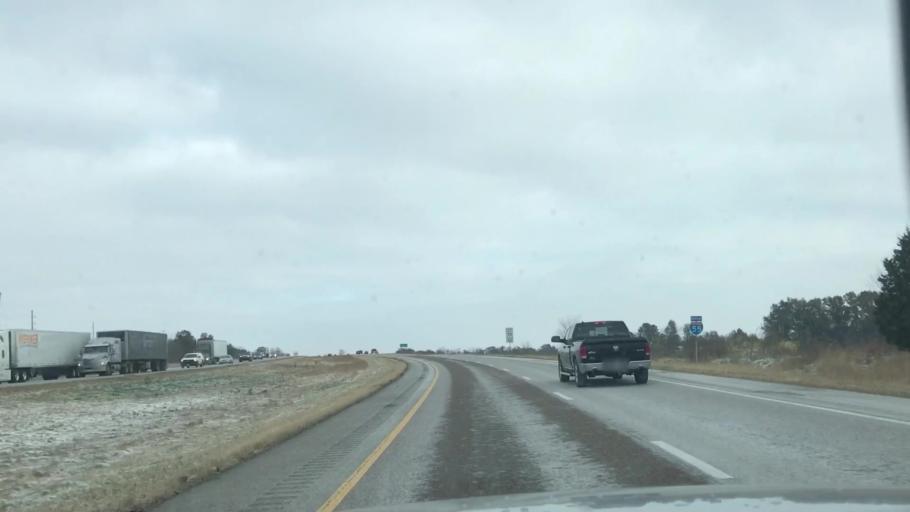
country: US
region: Illinois
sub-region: Macoupin County
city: Staunton
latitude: 38.9735
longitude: -89.7492
